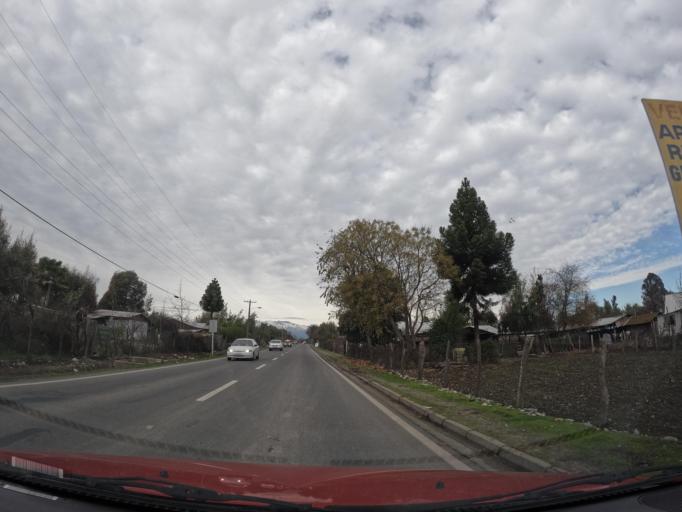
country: CL
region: Maule
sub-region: Provincia de Linares
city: Linares
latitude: -35.8830
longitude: -71.5386
